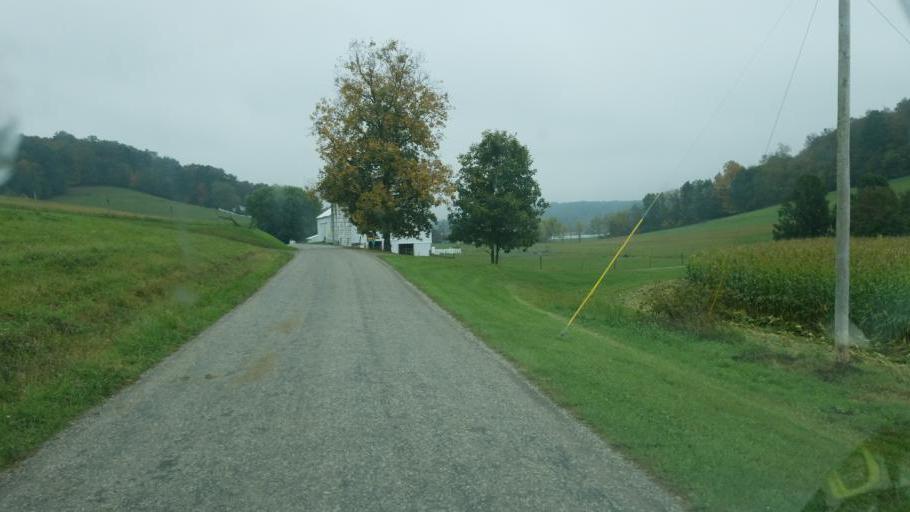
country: US
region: Ohio
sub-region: Tuscarawas County
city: Sugarcreek
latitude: 40.5720
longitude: -81.6995
